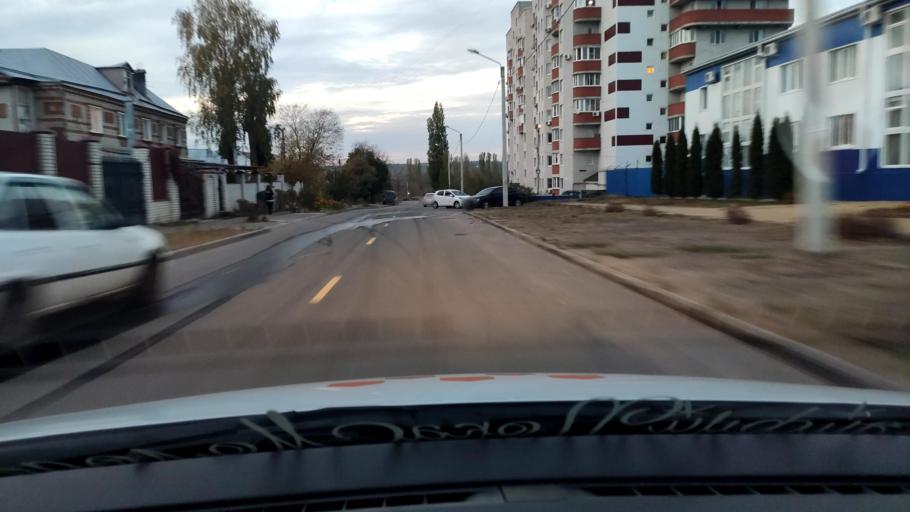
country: RU
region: Voronezj
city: Pridonskoy
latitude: 51.6617
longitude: 39.1241
